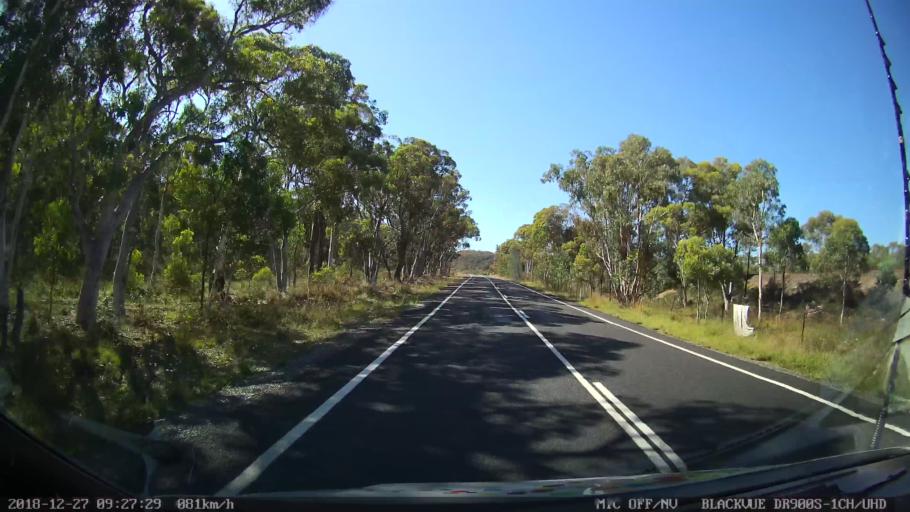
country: AU
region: New South Wales
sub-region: Lithgow
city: Portland
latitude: -33.1532
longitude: 149.9938
